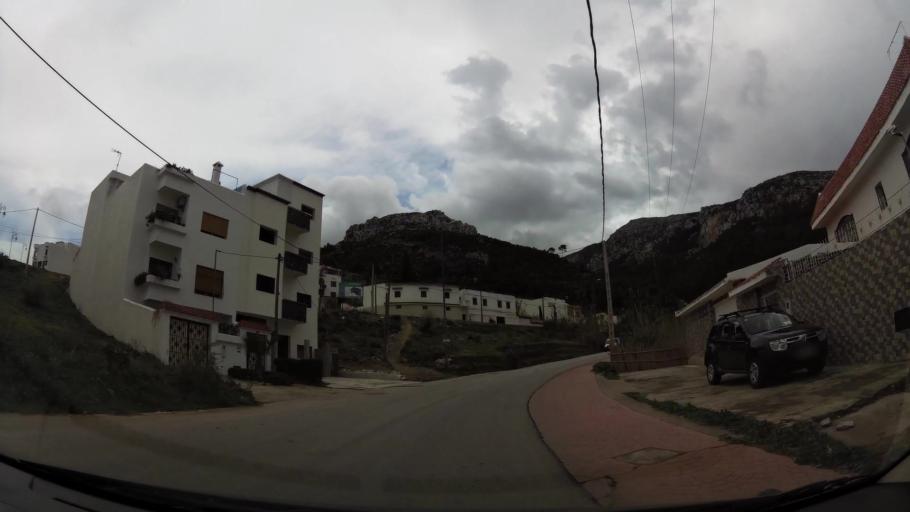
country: MA
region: Tanger-Tetouan
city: Tetouan
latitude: 35.5493
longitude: -5.3694
